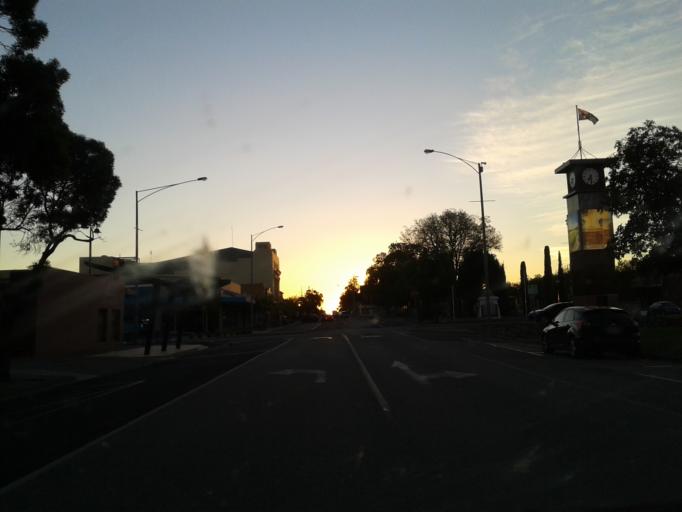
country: AU
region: Victoria
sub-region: Swan Hill
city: Swan Hill
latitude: -35.3386
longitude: 143.5602
